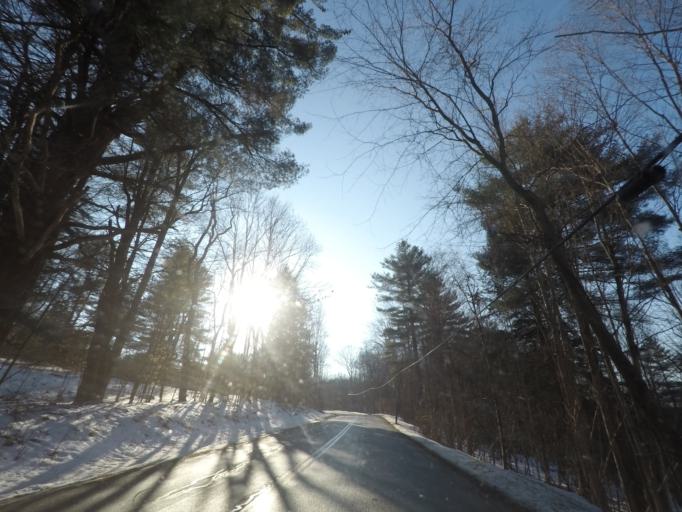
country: US
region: Massachusetts
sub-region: Berkshire County
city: Richmond
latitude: 42.5075
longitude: -73.4300
